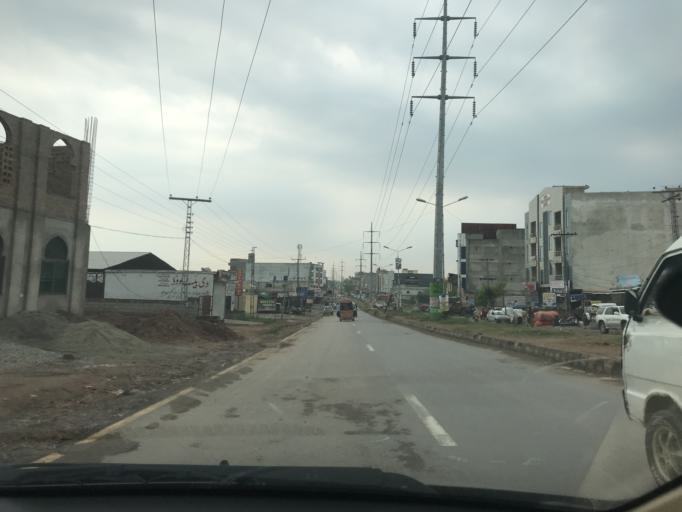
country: PK
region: Islamabad
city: Islamabad
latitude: 33.6842
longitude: 73.1603
